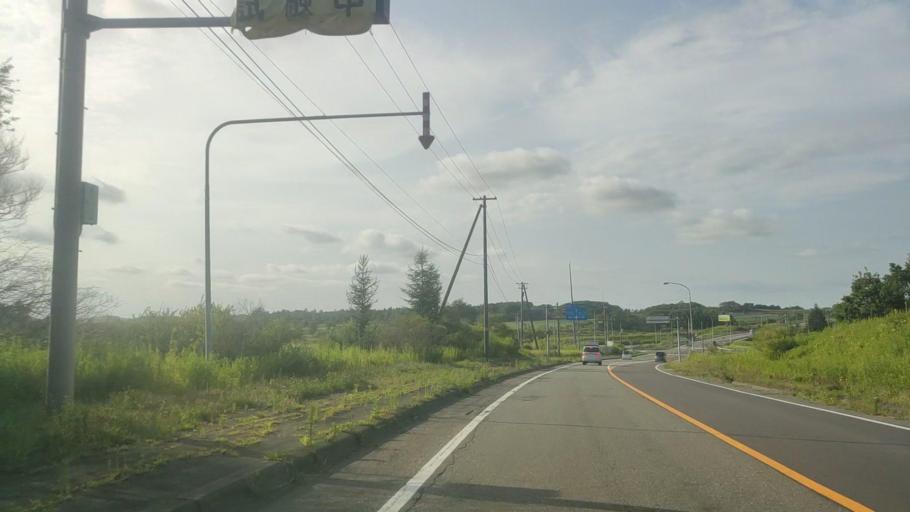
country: JP
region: Hokkaido
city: Chitose
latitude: 42.8838
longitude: 141.8128
